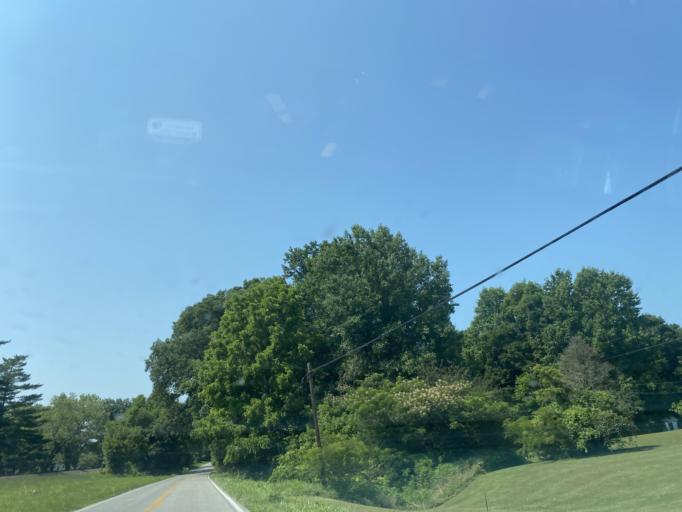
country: US
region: Kentucky
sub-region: Campbell County
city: Claryville
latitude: 38.8817
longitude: -84.4492
